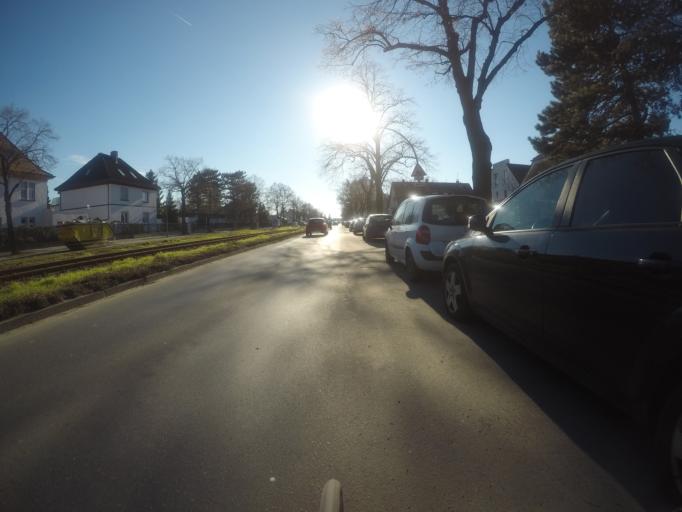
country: DE
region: Berlin
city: Rudow
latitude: 52.4268
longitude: 13.4887
